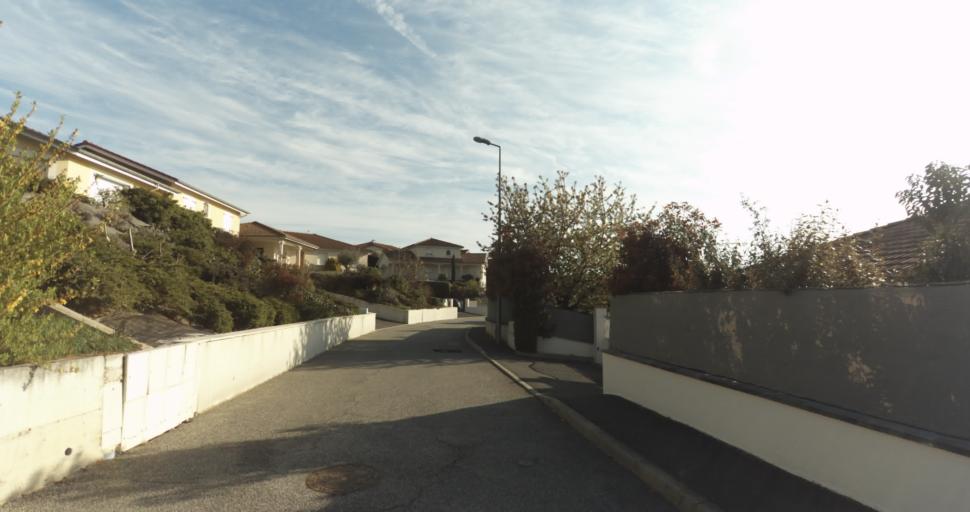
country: FR
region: Rhone-Alpes
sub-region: Departement de la Loire
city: Saint-Jean-Bonnefonds
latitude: 45.4475
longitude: 4.4458
